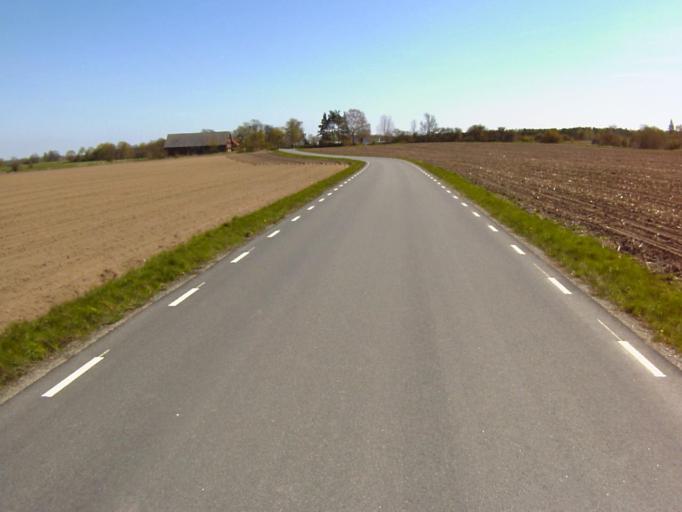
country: SE
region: Skane
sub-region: Kristianstads Kommun
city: Norra Asum
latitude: 55.9922
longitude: 14.1048
